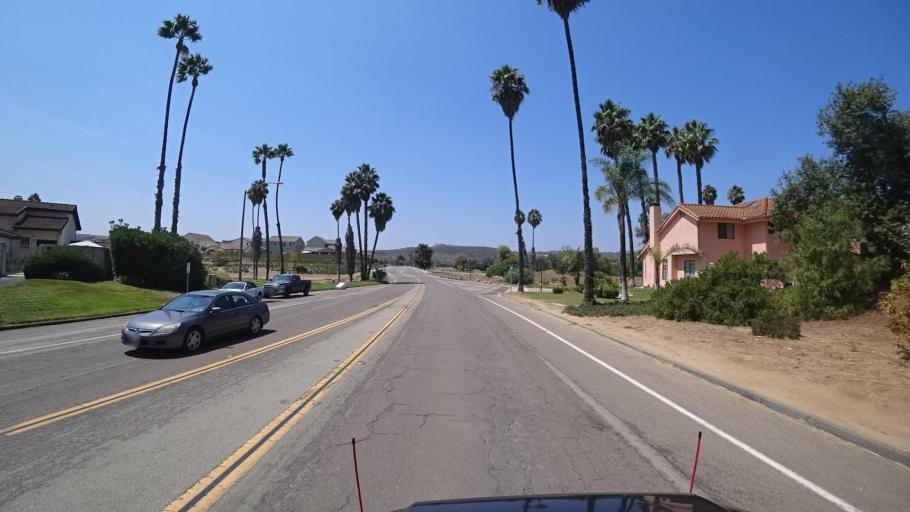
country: US
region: California
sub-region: San Diego County
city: Bonsall
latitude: 33.2904
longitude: -117.2160
